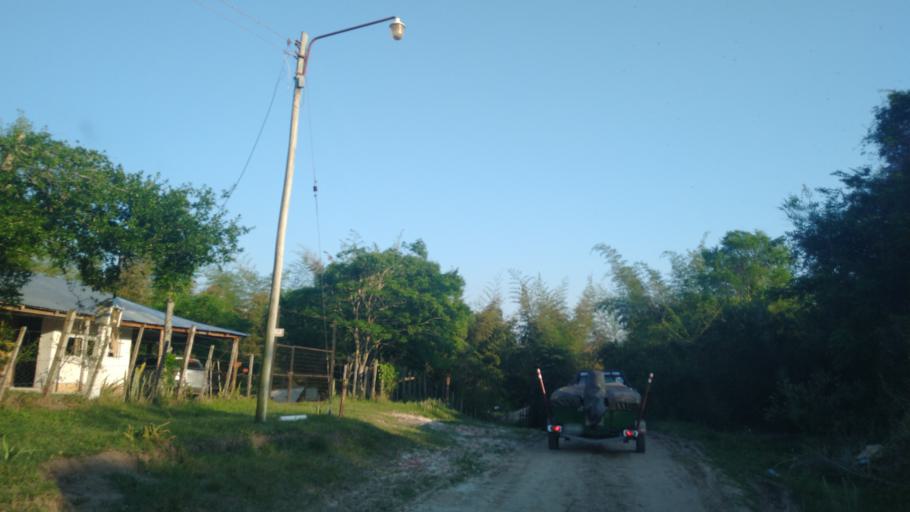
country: PY
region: Neembucu
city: Cerrito
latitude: -27.3712
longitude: -57.6561
